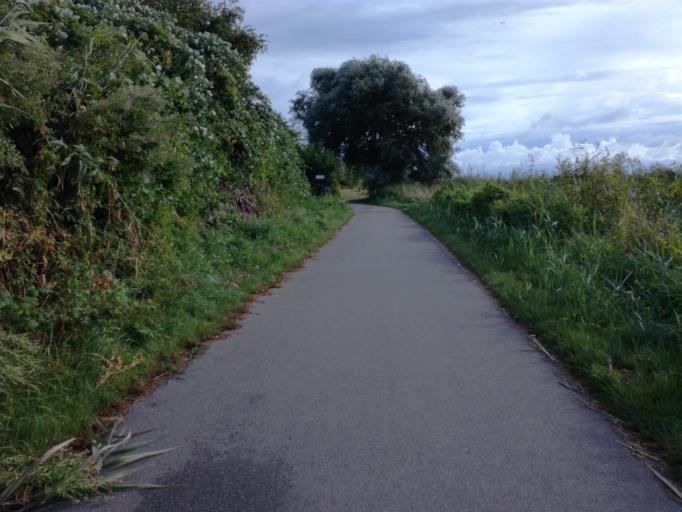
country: DK
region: South Denmark
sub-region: Fredericia Kommune
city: Fredericia
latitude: 55.5729
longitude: 9.7747
